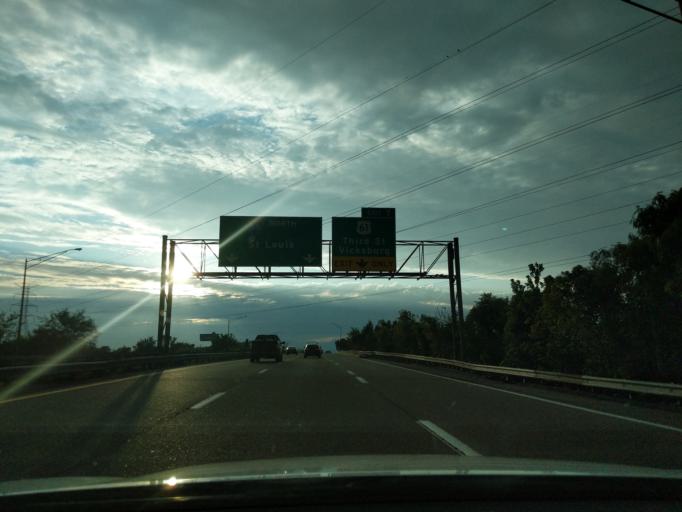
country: US
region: Tennessee
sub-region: Shelby County
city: New South Memphis
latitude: 35.0759
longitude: -90.0416
